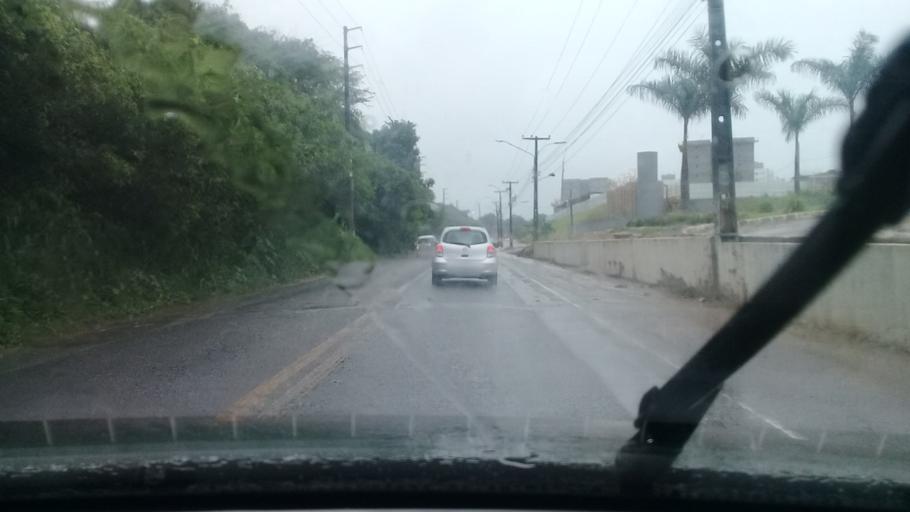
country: BR
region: Pernambuco
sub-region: Paulista
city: Paulista
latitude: -7.9485
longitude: -34.8847
